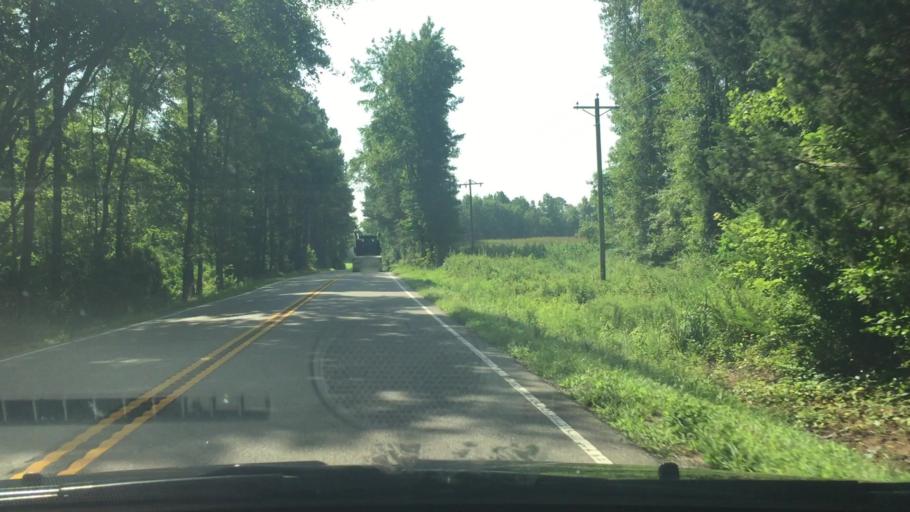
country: US
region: Virginia
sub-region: Sussex County
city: Sussex
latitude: 37.0215
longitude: -77.2874
